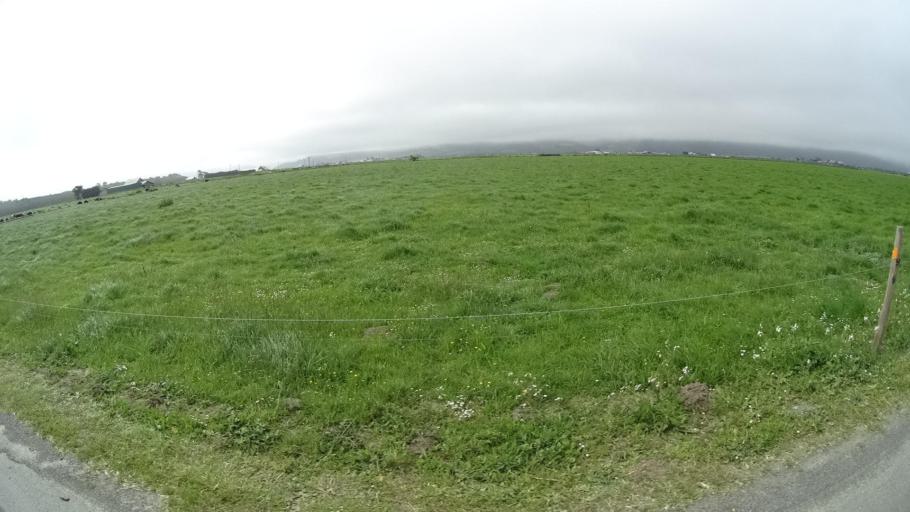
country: US
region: California
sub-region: Humboldt County
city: Fortuna
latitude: 40.5916
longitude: -124.1937
